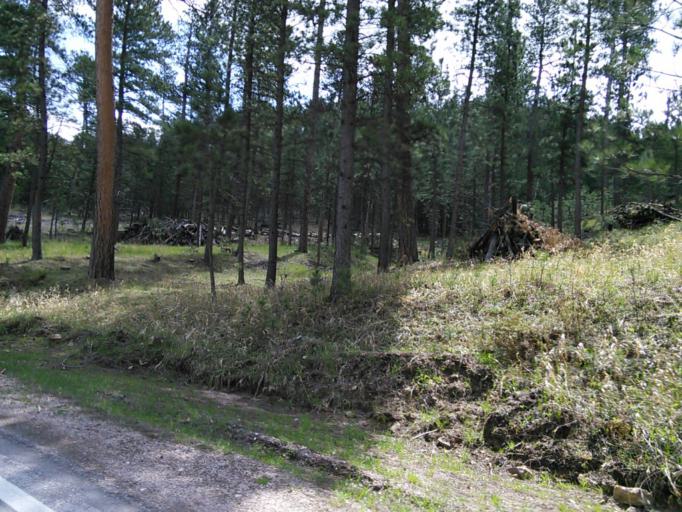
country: US
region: South Dakota
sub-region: Custer County
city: Custer
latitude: 43.7986
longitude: -103.4386
